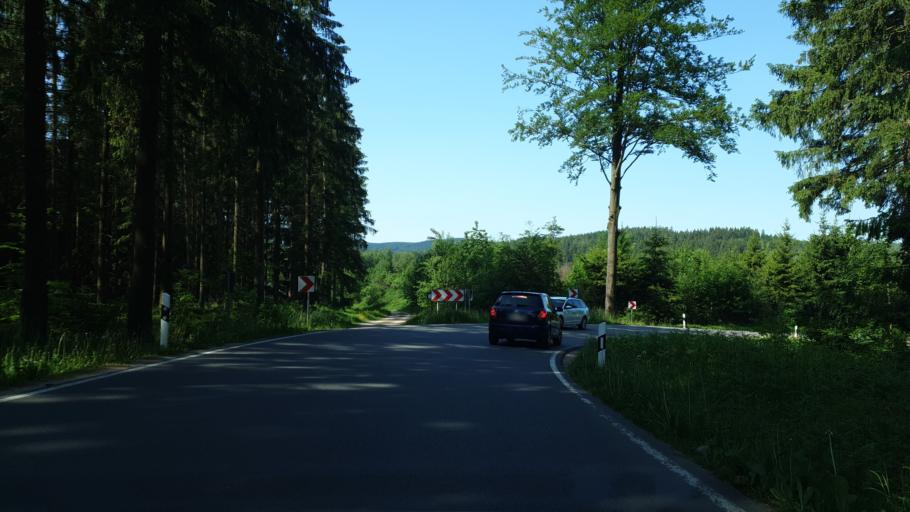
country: DE
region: Saxony
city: Eibenstock
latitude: 50.5253
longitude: 12.6169
